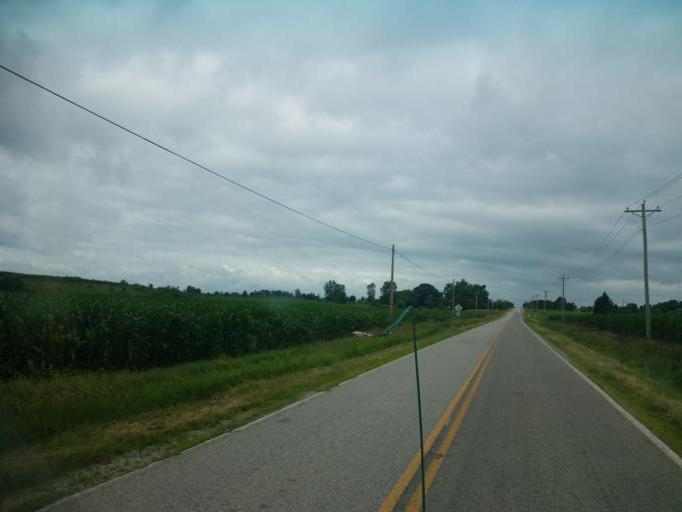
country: US
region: Ohio
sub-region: Union County
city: Richwood
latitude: 40.4150
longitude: -83.4696
